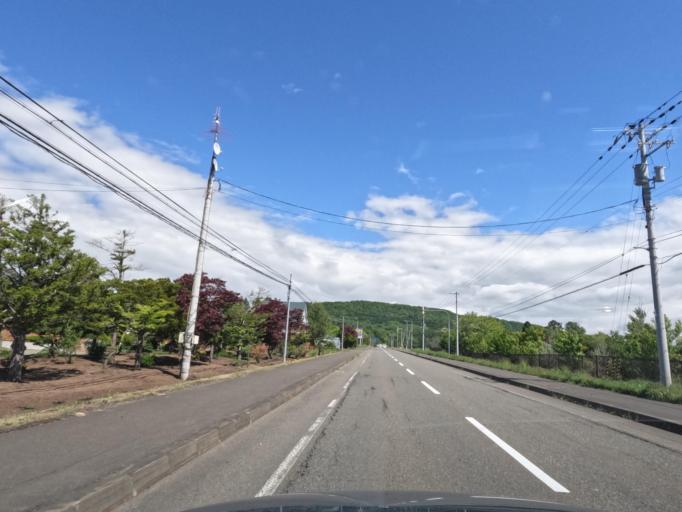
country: JP
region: Hokkaido
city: Kitahiroshima
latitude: 42.9985
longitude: 141.7251
